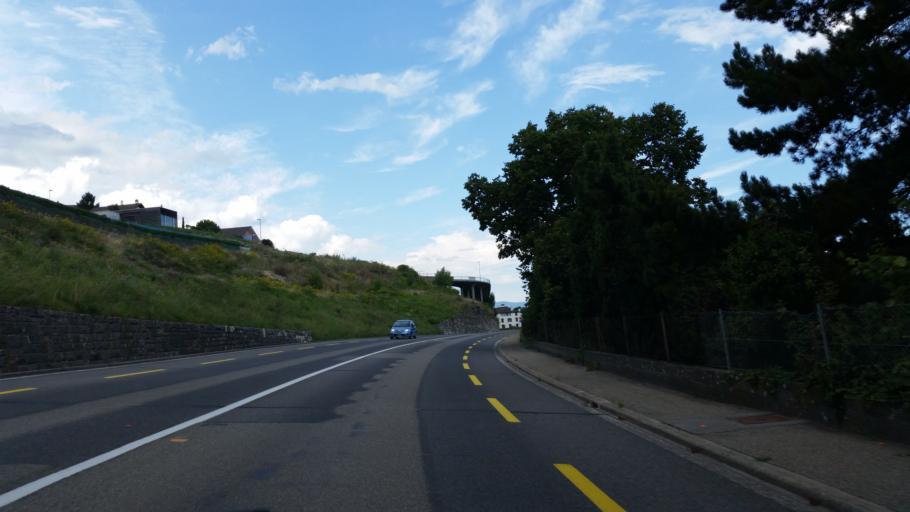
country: CH
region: Neuchatel
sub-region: Boudry District
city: Saint-Aubin-Sauges
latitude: 46.8852
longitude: 6.7637
